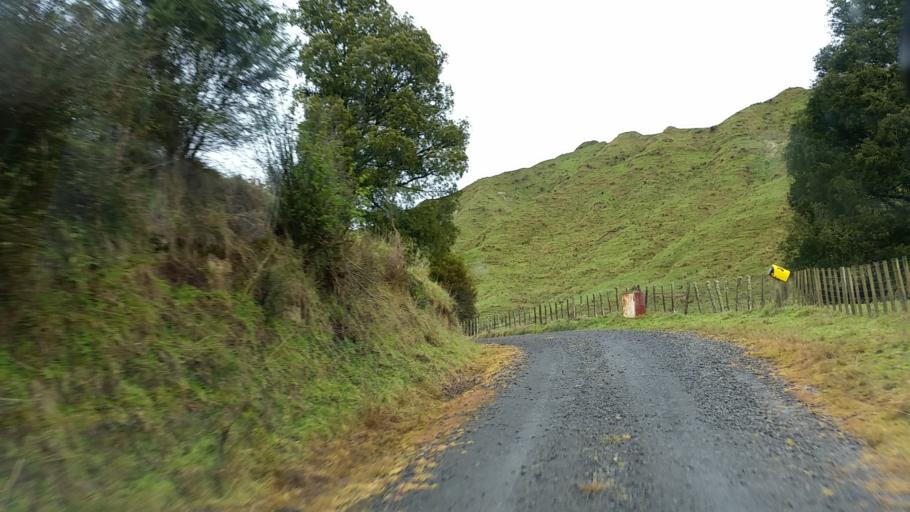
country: NZ
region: Taranaki
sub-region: South Taranaki District
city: Eltham
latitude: -39.4840
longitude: 174.4358
